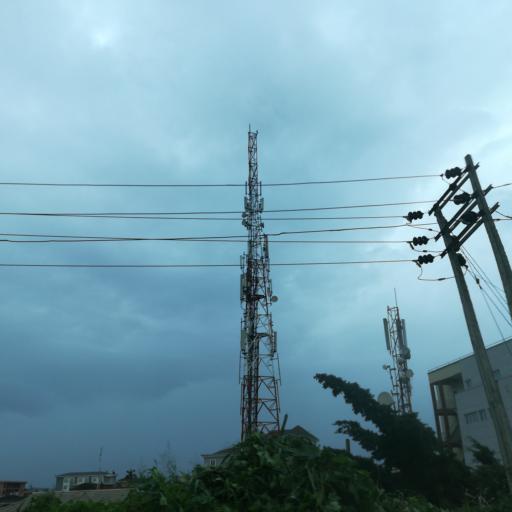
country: NG
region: Lagos
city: Oshodi
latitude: 6.5492
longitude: 3.3346
